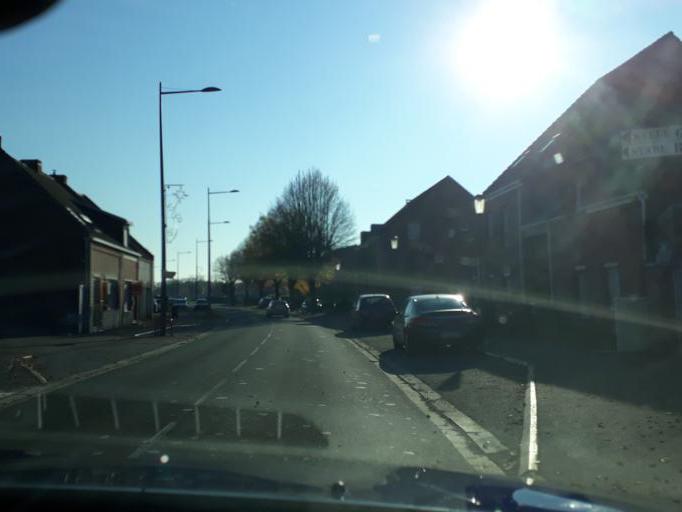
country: FR
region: Nord-Pas-de-Calais
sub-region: Departement du Nord
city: Masny
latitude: 50.3440
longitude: 3.2014
